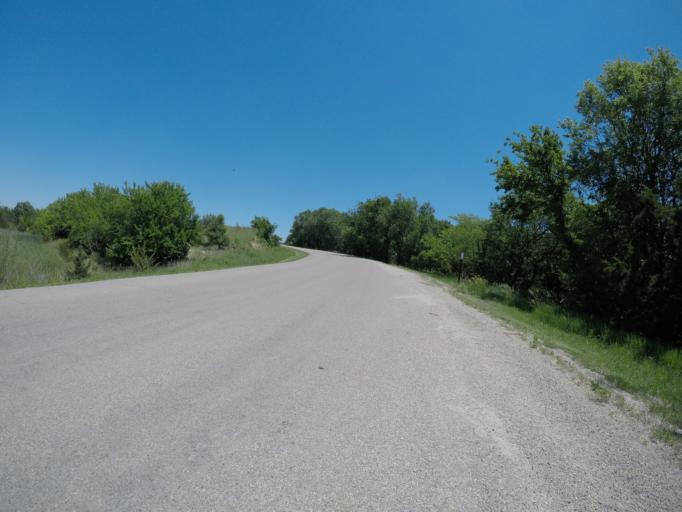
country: US
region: Kansas
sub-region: Geary County
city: Junction City
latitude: 38.9870
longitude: -96.8222
